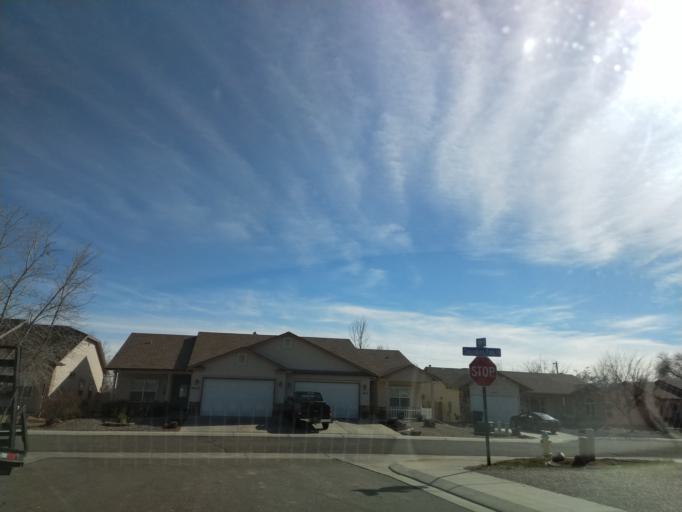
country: US
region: Colorado
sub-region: Mesa County
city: Grand Junction
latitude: 39.0830
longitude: -108.5306
